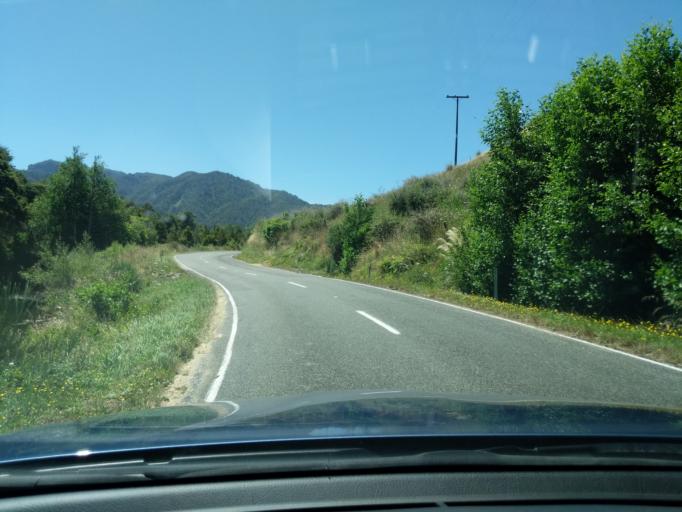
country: NZ
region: Tasman
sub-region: Tasman District
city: Takaka
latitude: -40.7351
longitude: 172.5819
